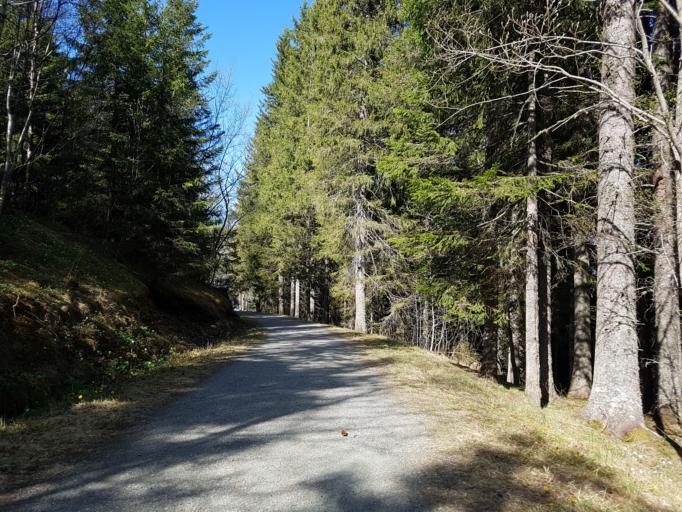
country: NO
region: Sor-Trondelag
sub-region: Trondheim
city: Trondheim
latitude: 63.4472
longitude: 10.3014
